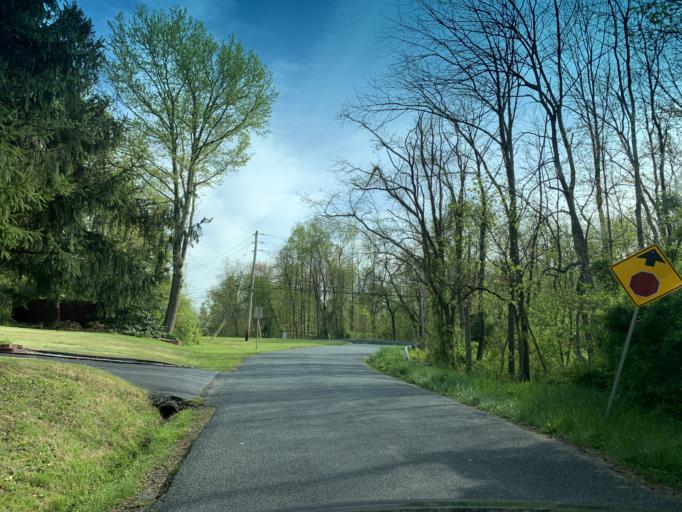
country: US
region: Maryland
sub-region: Harford County
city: Perryman
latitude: 39.4768
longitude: -76.2030
